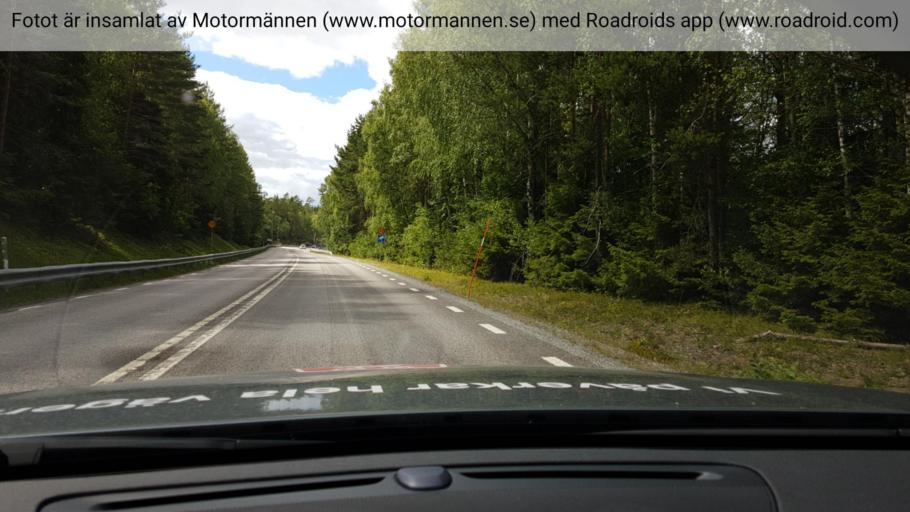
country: SE
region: Stockholm
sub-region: Osterakers Kommun
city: Akersberga
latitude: 59.4283
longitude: 18.2327
